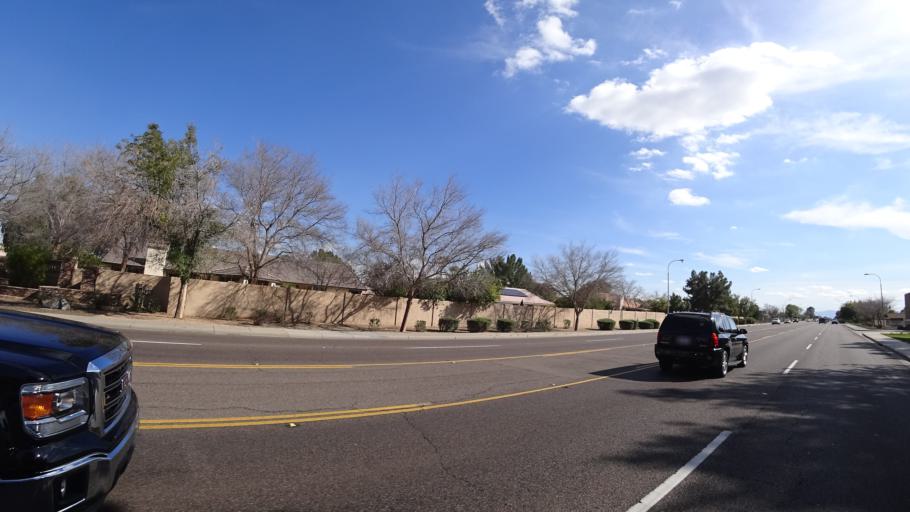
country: US
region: Arizona
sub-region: Maricopa County
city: Peoria
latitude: 33.6206
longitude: -112.2201
